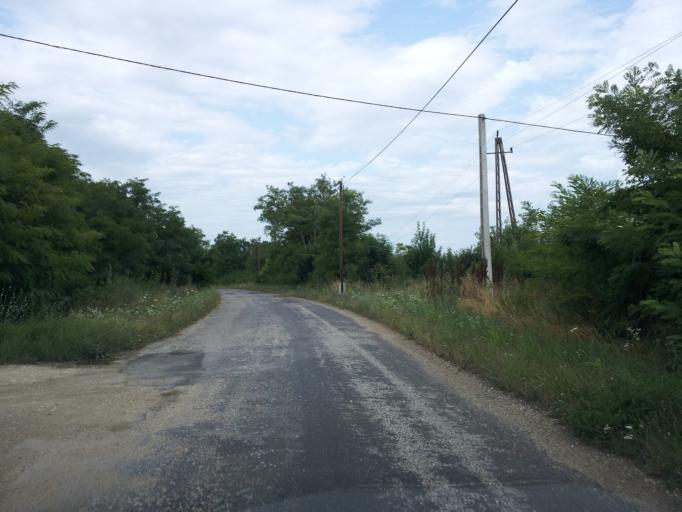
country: HU
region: Fejer
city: Enying
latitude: 46.9170
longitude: 18.2362
